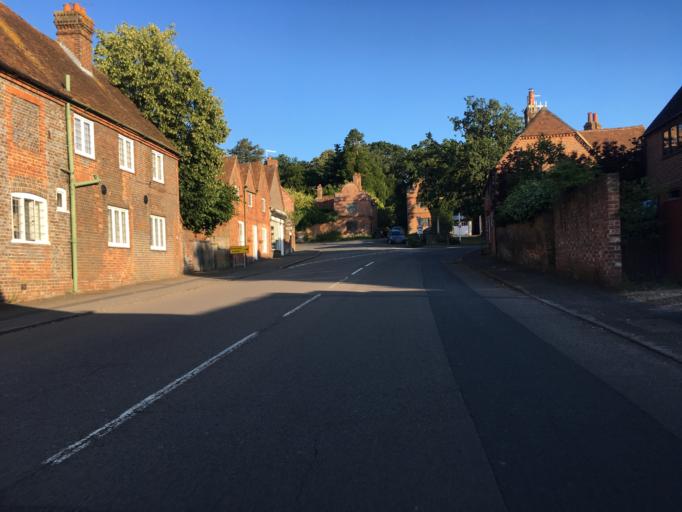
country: GB
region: England
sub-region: Hampshire
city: Tadley
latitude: 51.3825
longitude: -1.1522
